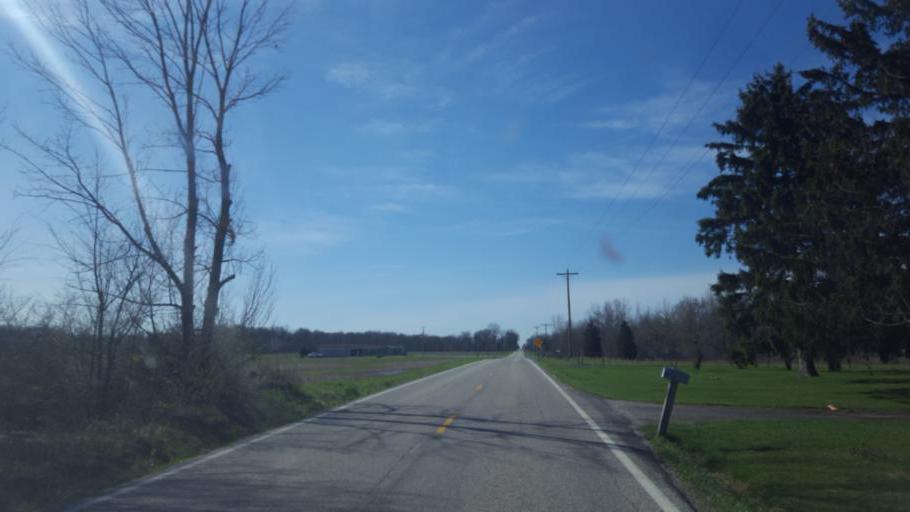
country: US
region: Ohio
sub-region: Morrow County
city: Cardington
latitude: 40.5453
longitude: -82.9624
